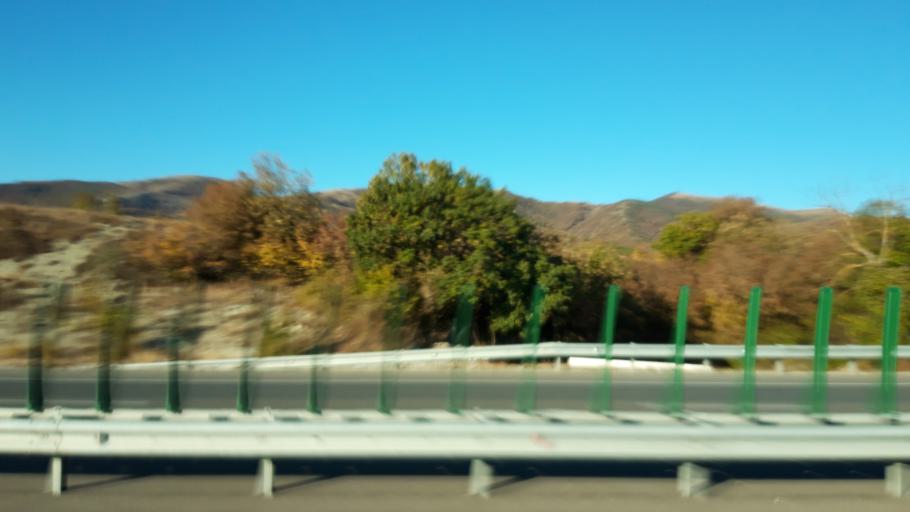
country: RU
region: Krasnodarskiy
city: Kabardinka
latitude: 44.6412
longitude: 37.9774
